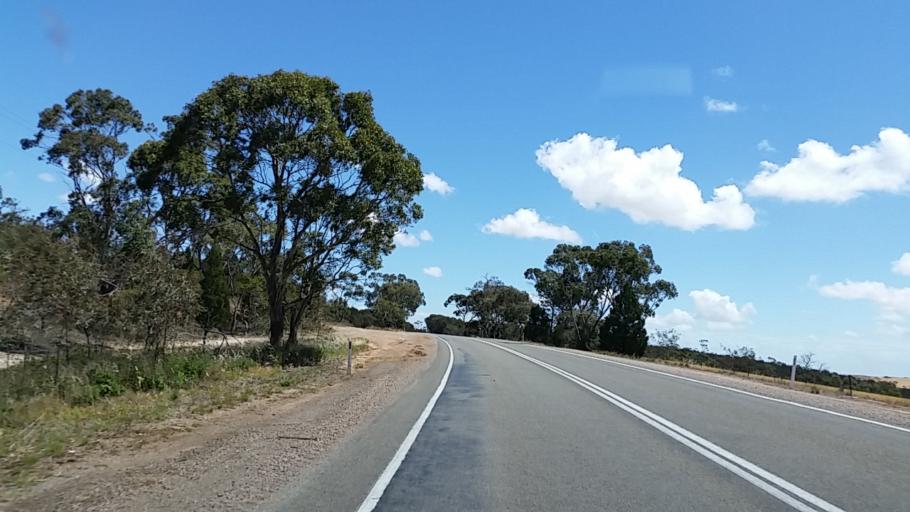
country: AU
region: South Australia
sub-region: Port Pirie City and Dists
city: Crystal Brook
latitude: -33.2838
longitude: 138.2636
